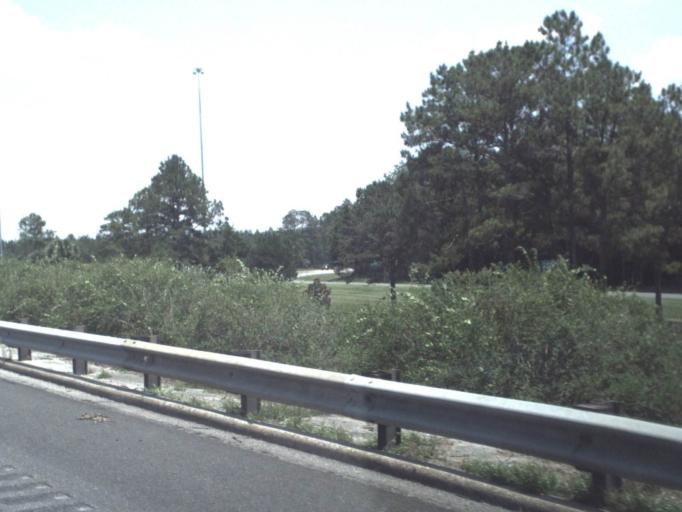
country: US
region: Florida
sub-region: Baker County
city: Macclenny
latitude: 30.2623
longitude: -82.1055
